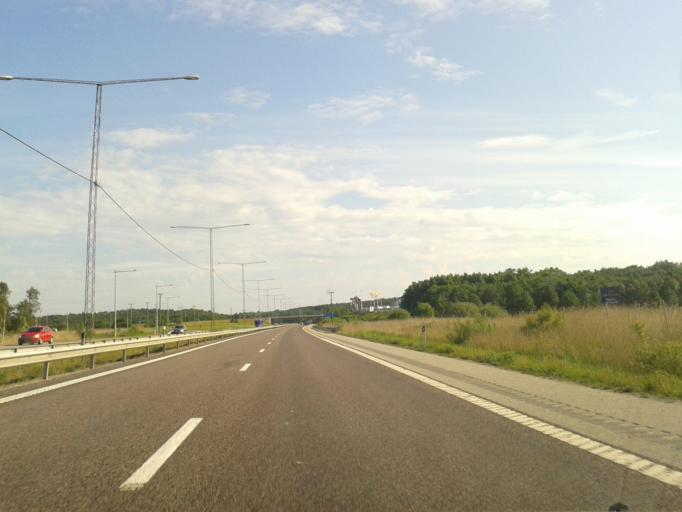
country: SE
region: Vaestra Goetaland
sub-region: Stenungsunds Kommun
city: Stora Hoga
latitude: 58.0204
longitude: 11.8445
